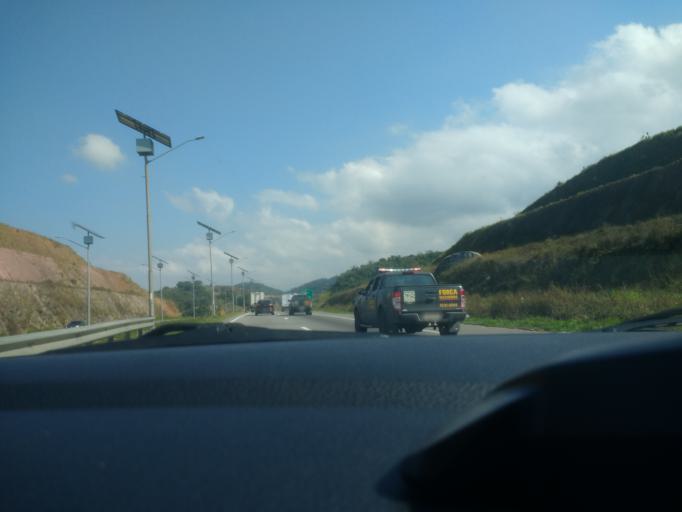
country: BR
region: Rio de Janeiro
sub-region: Nova Iguacu
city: Nova Iguacu
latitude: -22.6823
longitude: -43.4636
